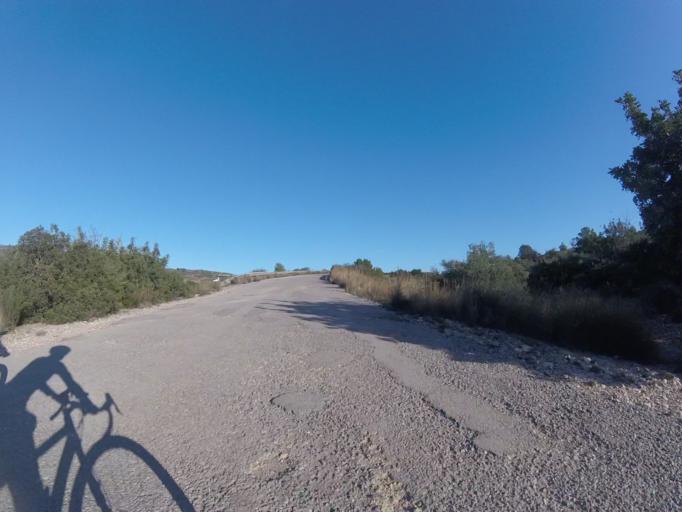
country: ES
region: Valencia
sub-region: Provincia de Castello
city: Torreblanca
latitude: 40.2248
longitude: 0.1982
